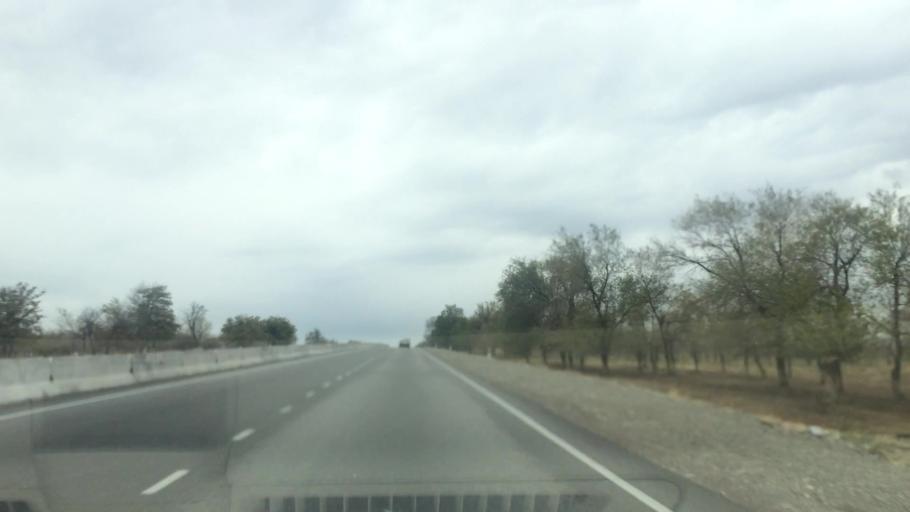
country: UZ
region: Samarqand
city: Bulung'ur
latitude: 39.9326
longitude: 67.5231
